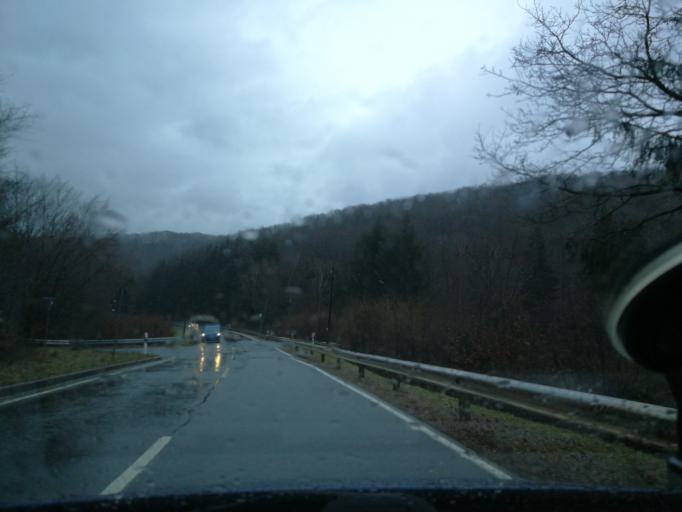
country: DE
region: Rheinland-Pfalz
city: Rorodt
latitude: 49.7601
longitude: 7.0640
